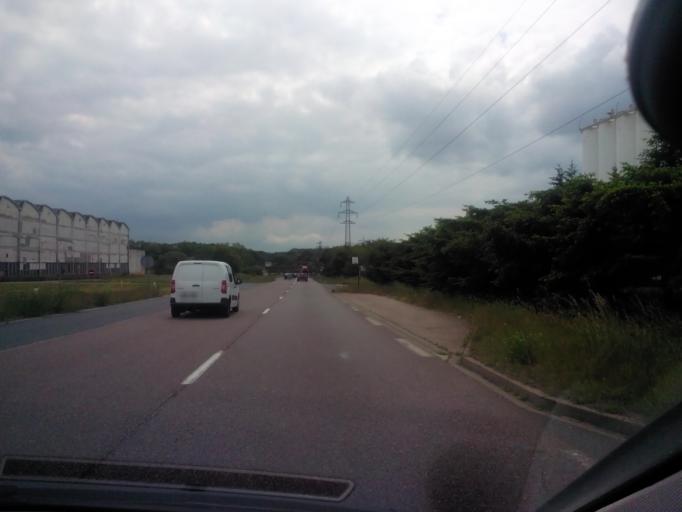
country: FR
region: Lorraine
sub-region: Departement de la Moselle
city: Carling
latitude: 49.1458
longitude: 6.7080
